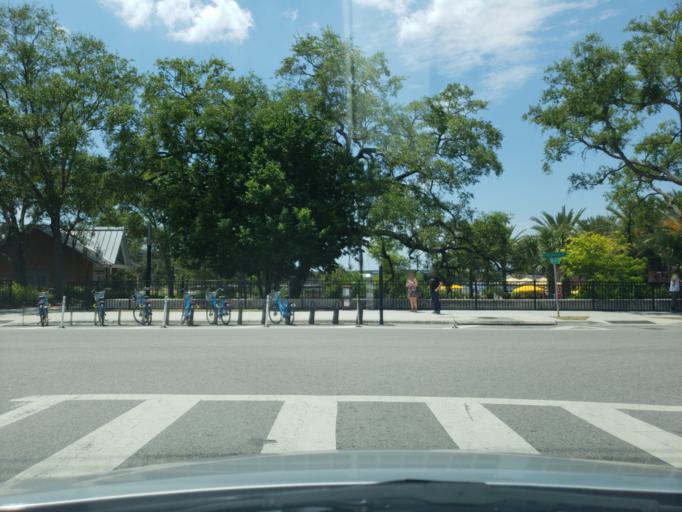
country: US
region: Florida
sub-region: Hillsborough County
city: Tampa
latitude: 27.9595
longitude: -82.4623
